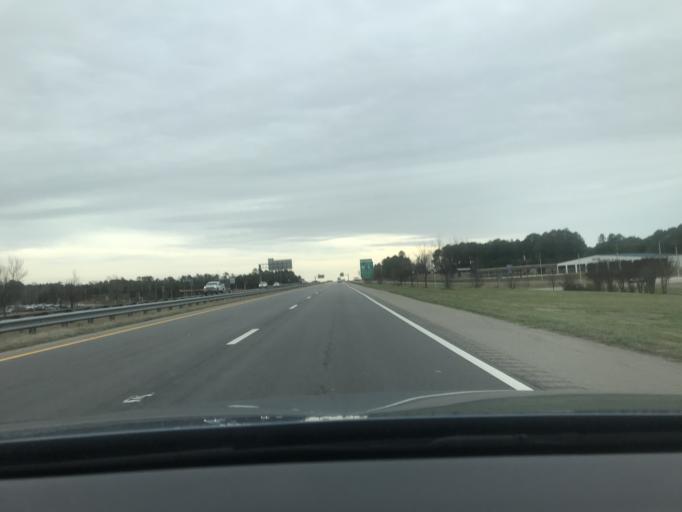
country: US
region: North Carolina
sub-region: Lee County
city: Sanford
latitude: 35.5257
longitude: -79.1832
